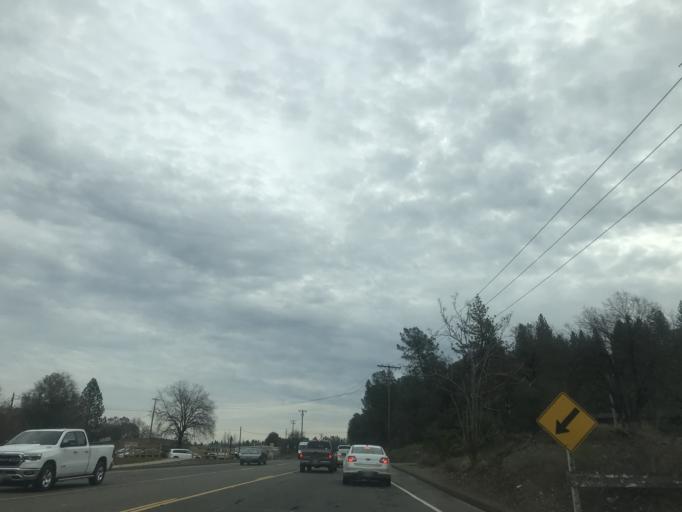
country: US
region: California
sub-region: El Dorado County
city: Diamond Springs
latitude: 38.7039
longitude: -120.8269
